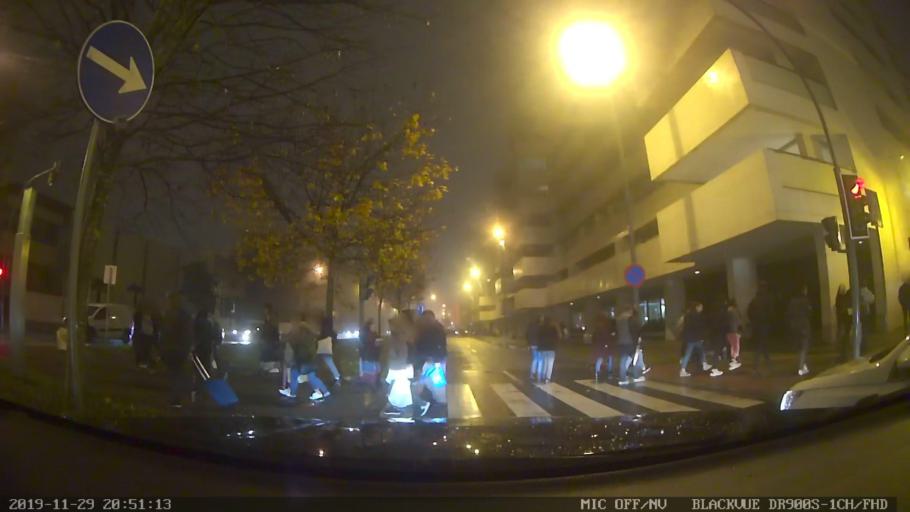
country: PT
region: Porto
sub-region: Matosinhos
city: Senhora da Hora
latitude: 41.1833
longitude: -8.6533
